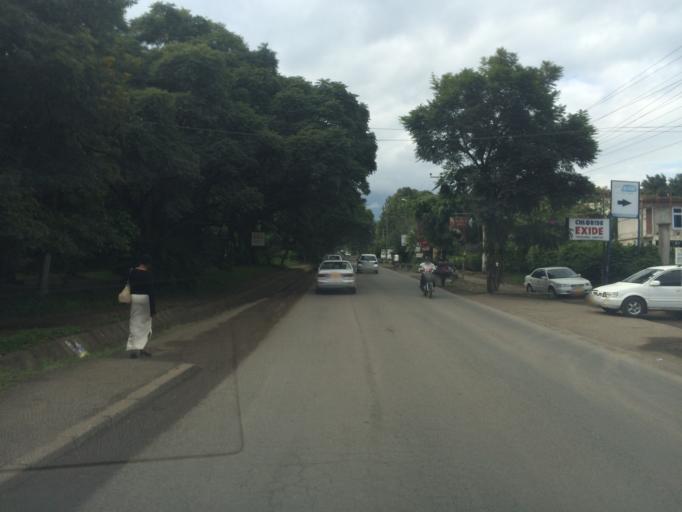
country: TZ
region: Arusha
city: Arusha
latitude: -3.3765
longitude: 36.7033
